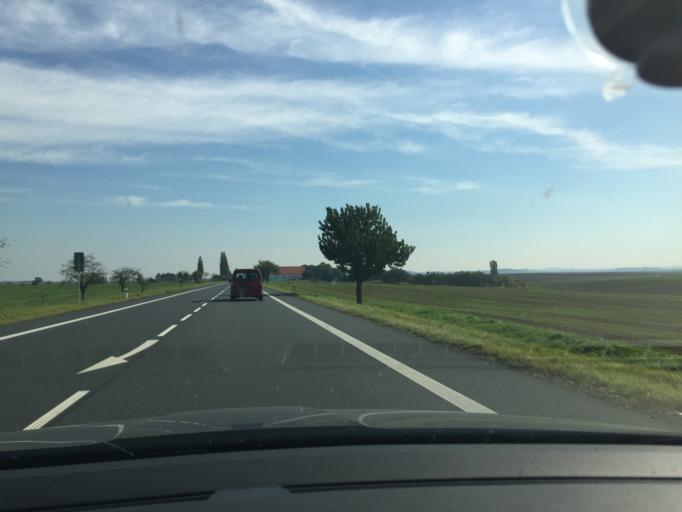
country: CZ
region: Central Bohemia
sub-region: Okres Kolin
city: Kourim
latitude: 50.0494
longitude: 14.9590
